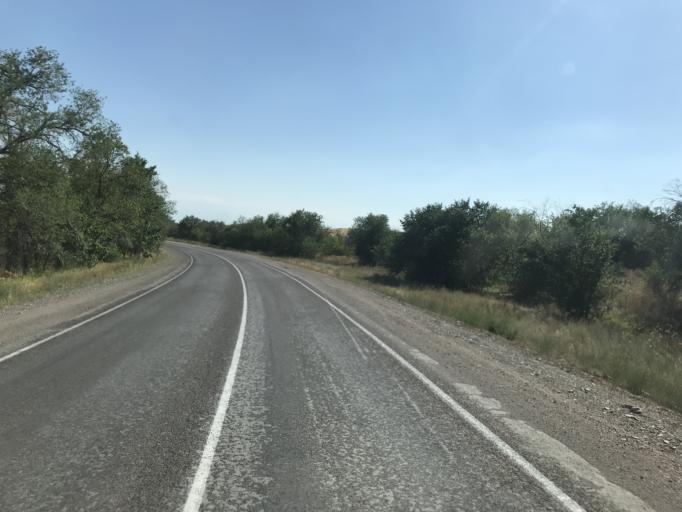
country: KZ
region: Zhambyl
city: Georgiyevka
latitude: 43.1571
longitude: 74.7065
